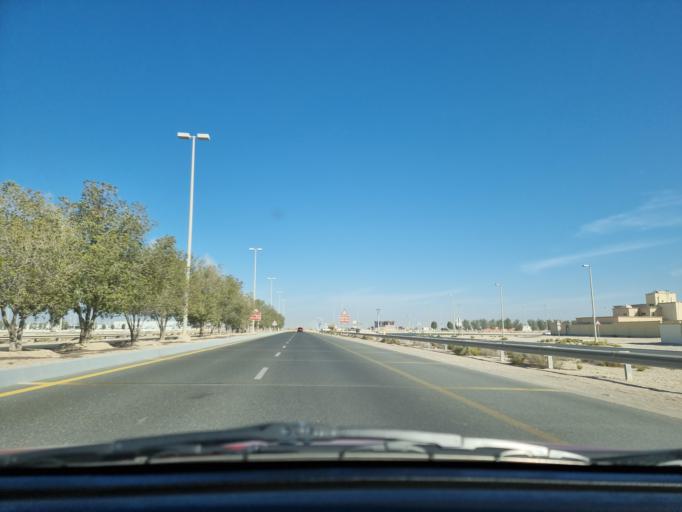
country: AE
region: Abu Dhabi
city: Abu Dhabi
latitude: 24.3955
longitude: 54.6940
